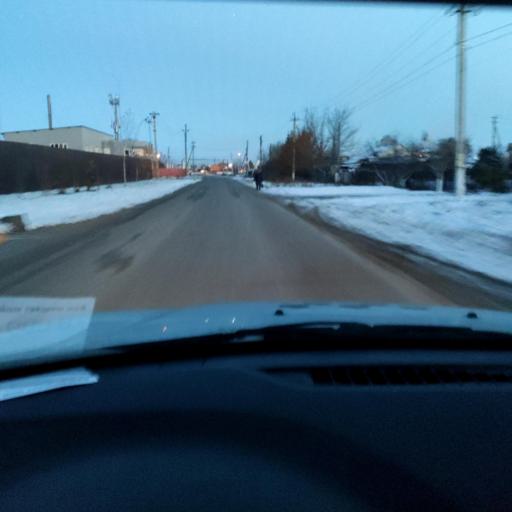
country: RU
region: Samara
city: Tol'yatti
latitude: 53.5692
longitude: 49.3927
